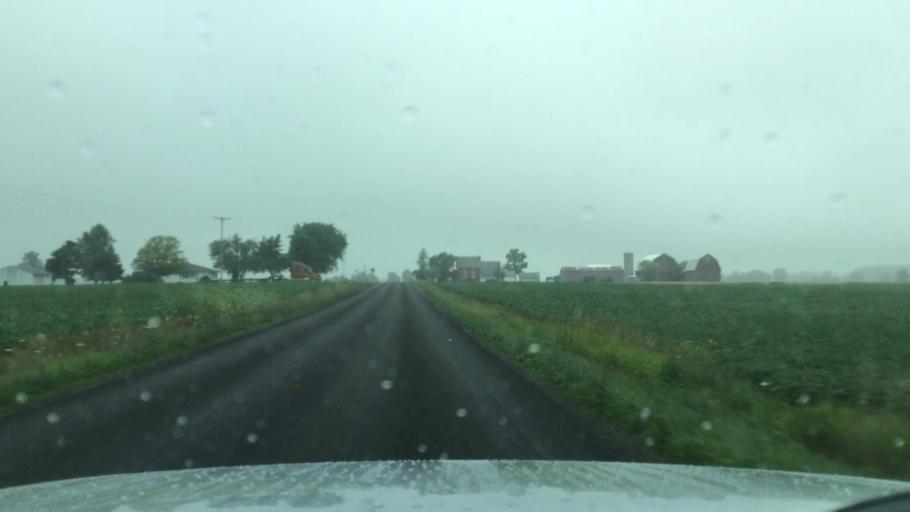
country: US
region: Michigan
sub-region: Shiawassee County
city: New Haven
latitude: 43.0574
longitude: -84.1258
